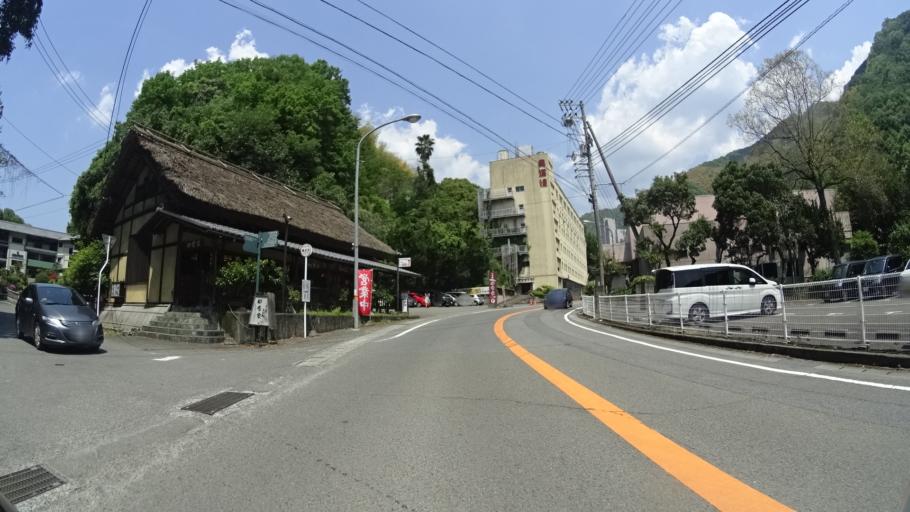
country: JP
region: Ehime
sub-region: Shikoku-chuo Shi
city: Matsuyama
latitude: 33.8650
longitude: 132.8232
